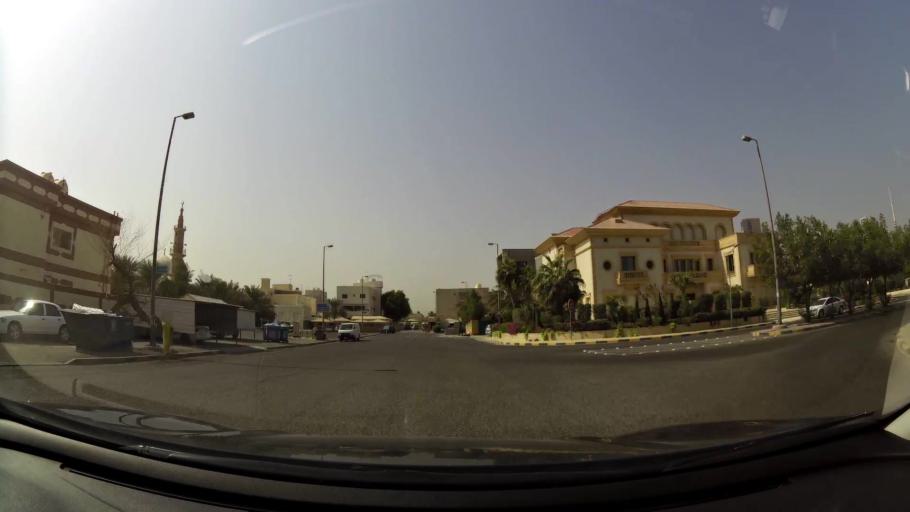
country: KW
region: Al Asimah
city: Ad Dasmah
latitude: 29.3614
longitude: 47.9917
